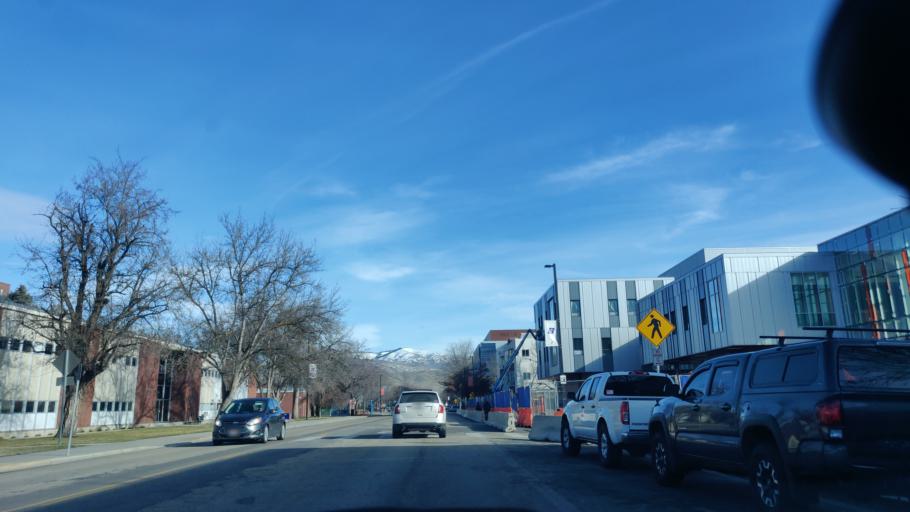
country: US
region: Idaho
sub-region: Ada County
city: Boise
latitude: 43.6010
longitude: -116.2002
